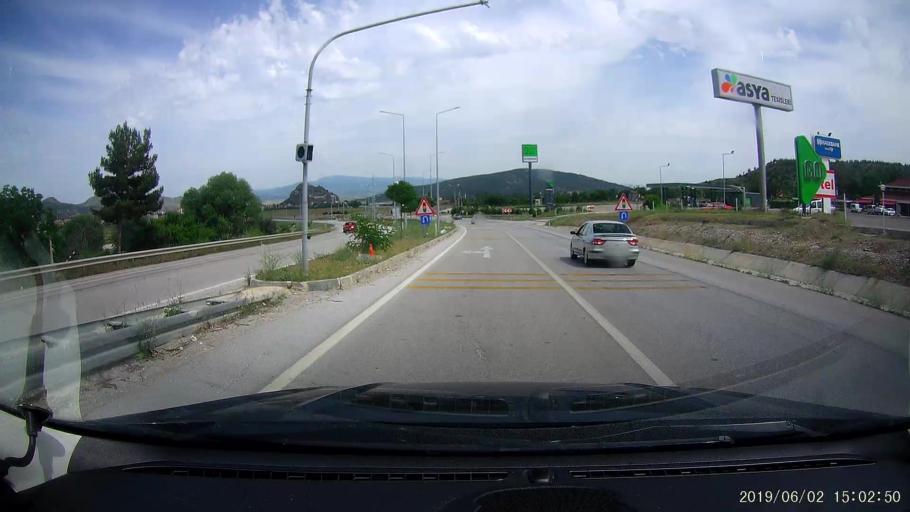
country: TR
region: Corum
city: Osmancik
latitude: 40.9781
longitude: 34.7723
